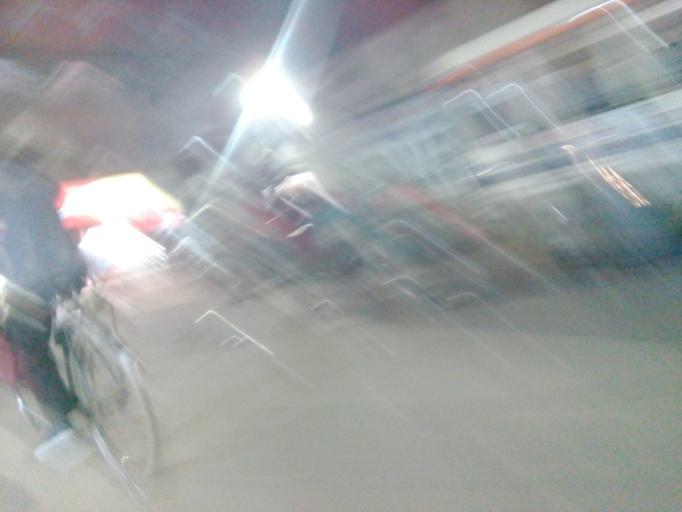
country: BD
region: Dhaka
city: Paltan
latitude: 23.7473
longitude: 90.4285
